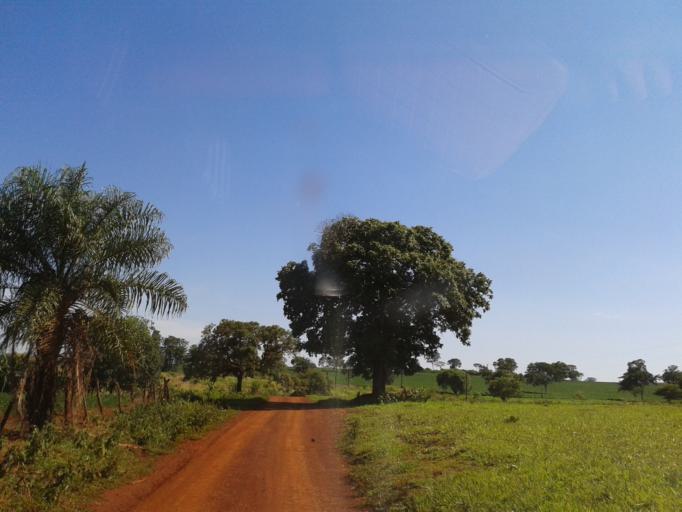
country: BR
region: Minas Gerais
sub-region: Centralina
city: Centralina
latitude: -18.6203
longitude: -49.2958
